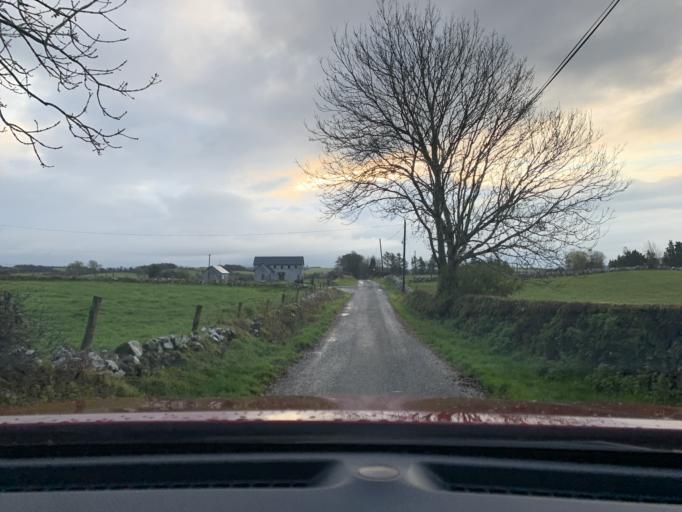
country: IE
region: Connaught
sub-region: Sligo
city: Ballymote
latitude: 54.0356
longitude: -8.5391
